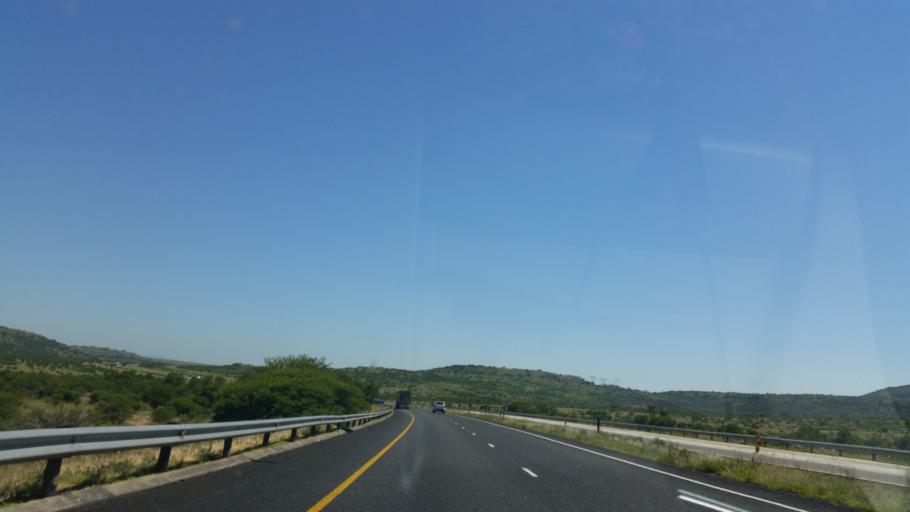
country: ZA
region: KwaZulu-Natal
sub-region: uThukela District Municipality
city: Ladysmith
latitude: -28.7001
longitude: 29.6397
